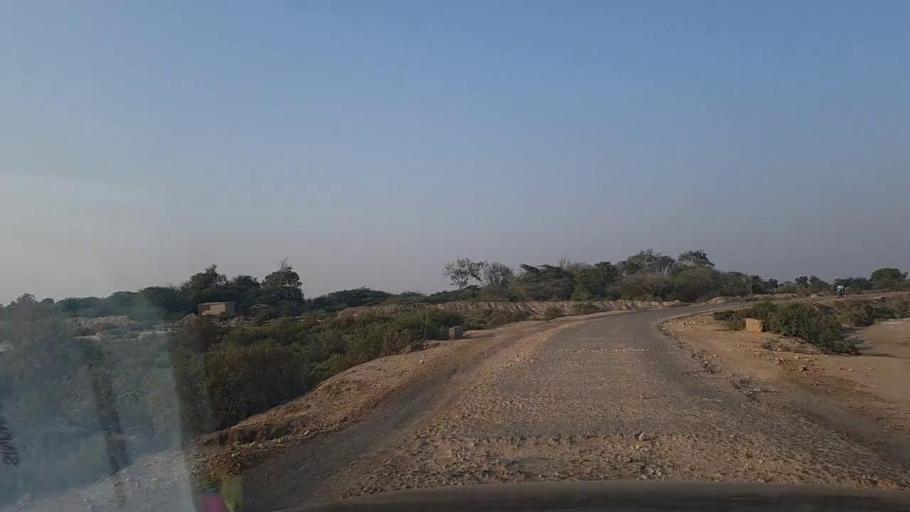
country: PK
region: Sindh
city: Keti Bandar
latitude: 24.2922
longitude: 67.5828
